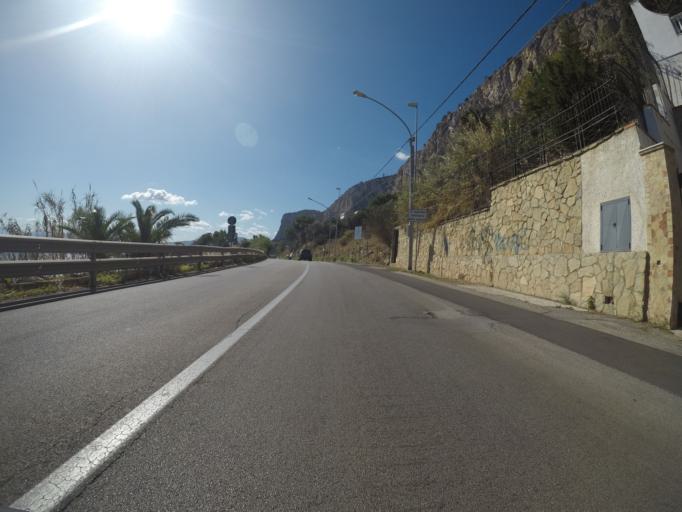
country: IT
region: Sicily
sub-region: Palermo
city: Palermo
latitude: 38.1776
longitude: 13.3660
